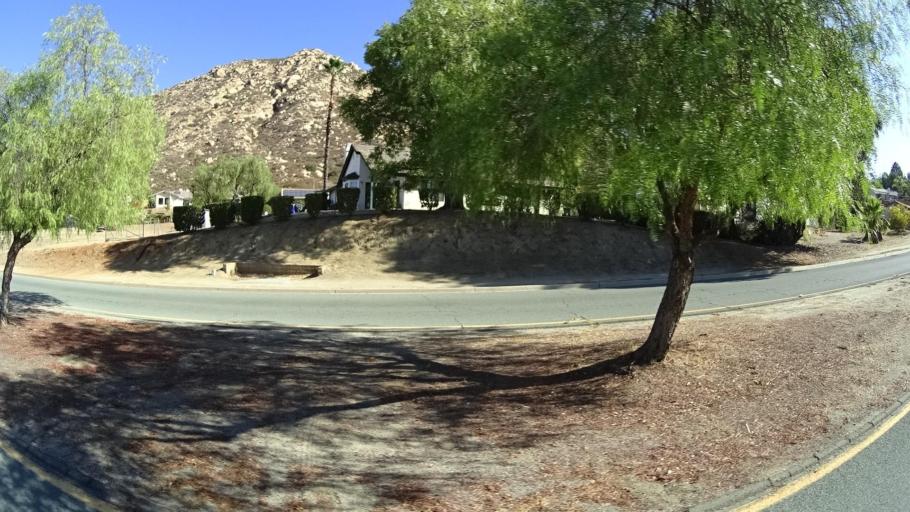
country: US
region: California
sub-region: San Diego County
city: San Diego Country Estates
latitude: 33.0033
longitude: -116.7748
